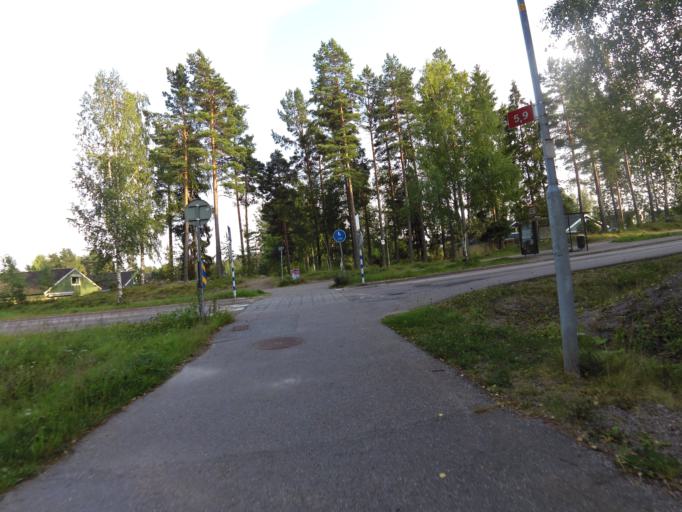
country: SE
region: Gaevleborg
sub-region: Gavle Kommun
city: Gavle
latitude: 60.6983
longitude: 17.0993
